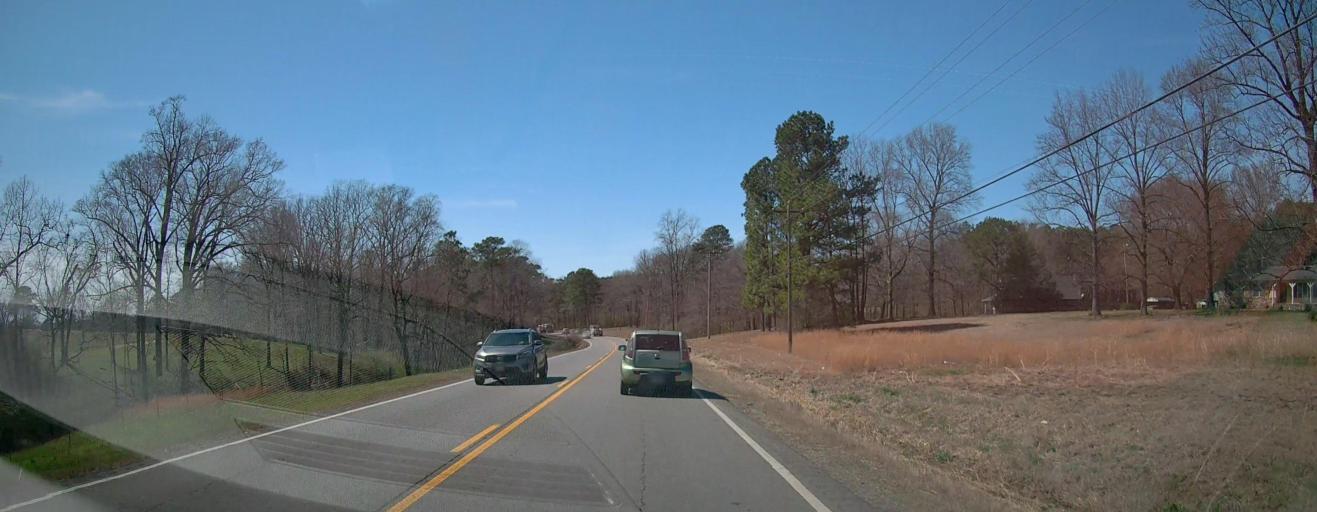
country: US
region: Alabama
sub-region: Blount County
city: Blountsville
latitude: 34.1754
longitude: -86.6728
